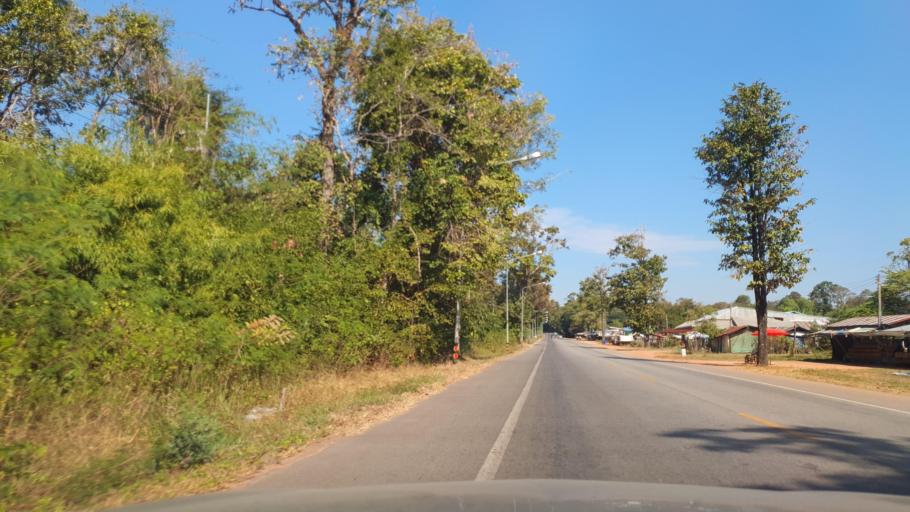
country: TH
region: Sakon Nakhon
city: Phu Phan
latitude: 17.0969
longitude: 103.9891
